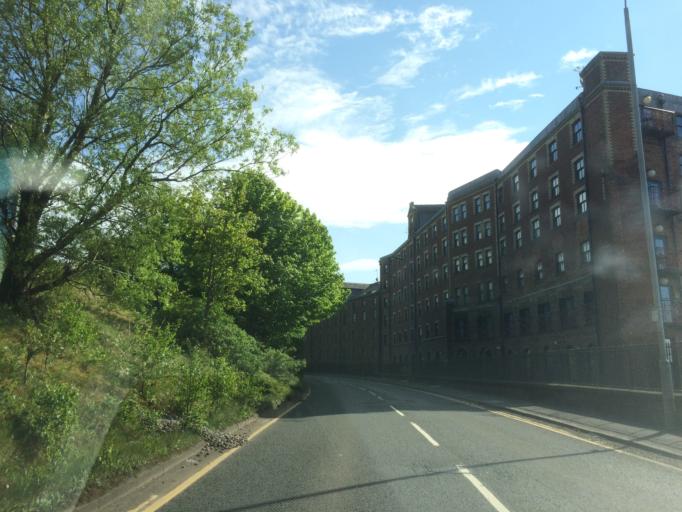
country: GB
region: Scotland
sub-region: Glasgow City
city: Glasgow
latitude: 55.8746
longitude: -4.2569
